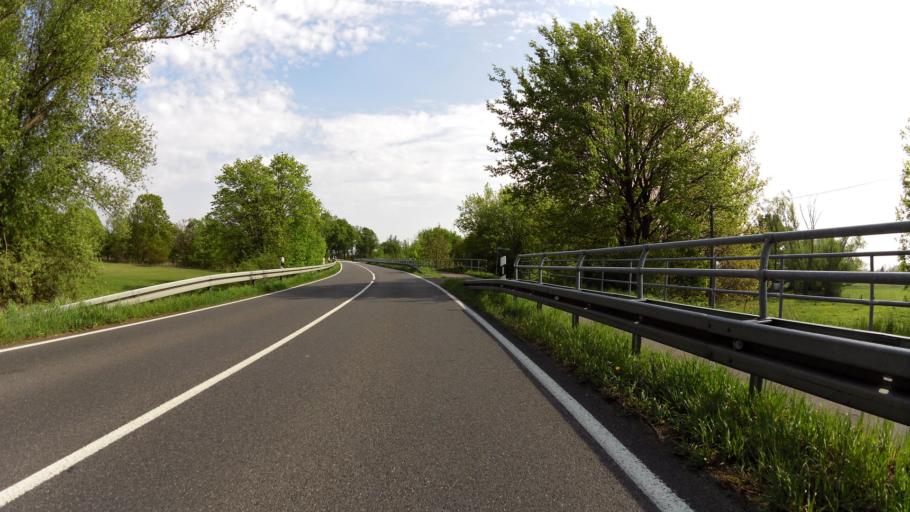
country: DE
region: Brandenburg
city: Spreenhagen
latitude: 52.3611
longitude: 13.8402
